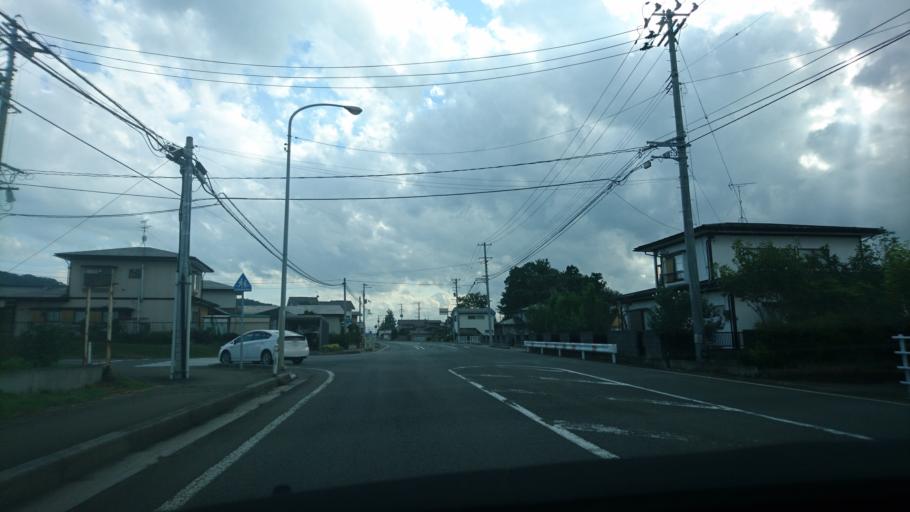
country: JP
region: Iwate
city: Kitakami
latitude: 39.2885
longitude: 141.1405
